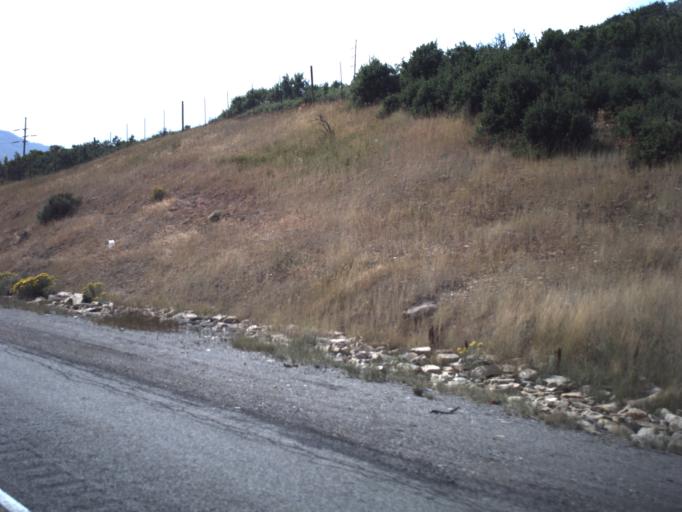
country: US
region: Utah
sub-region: Summit County
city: Summit Park
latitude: 40.7498
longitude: -111.6334
